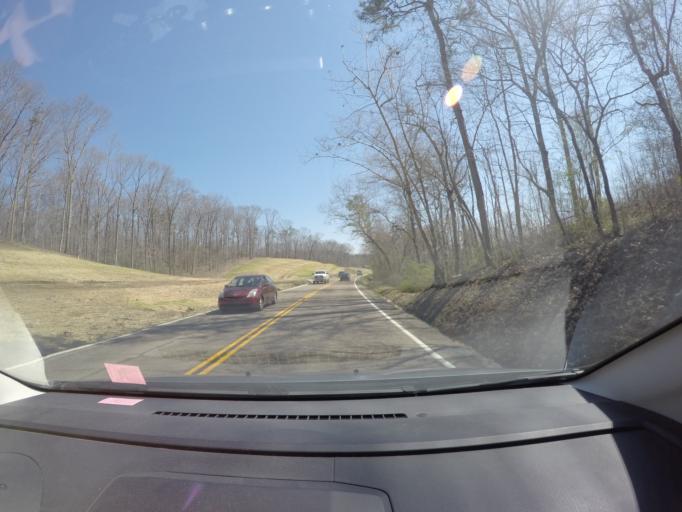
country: US
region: Tennessee
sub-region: Hamilton County
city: Collegedale
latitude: 35.0686
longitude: -85.0904
